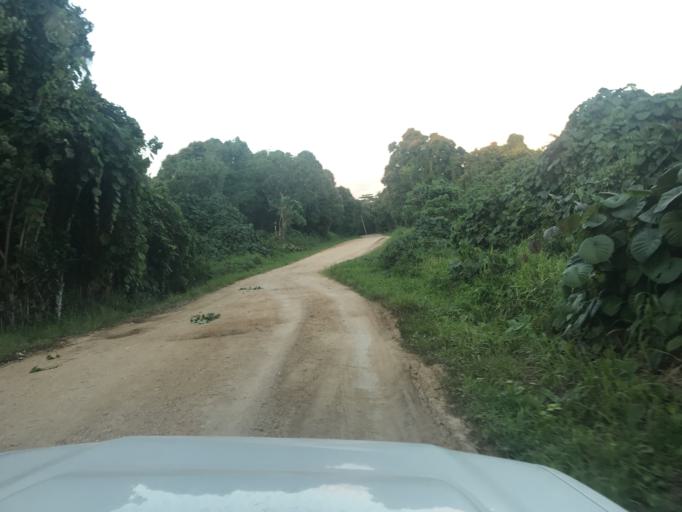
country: VU
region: Sanma
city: Luganville
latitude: -15.5608
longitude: 166.9630
